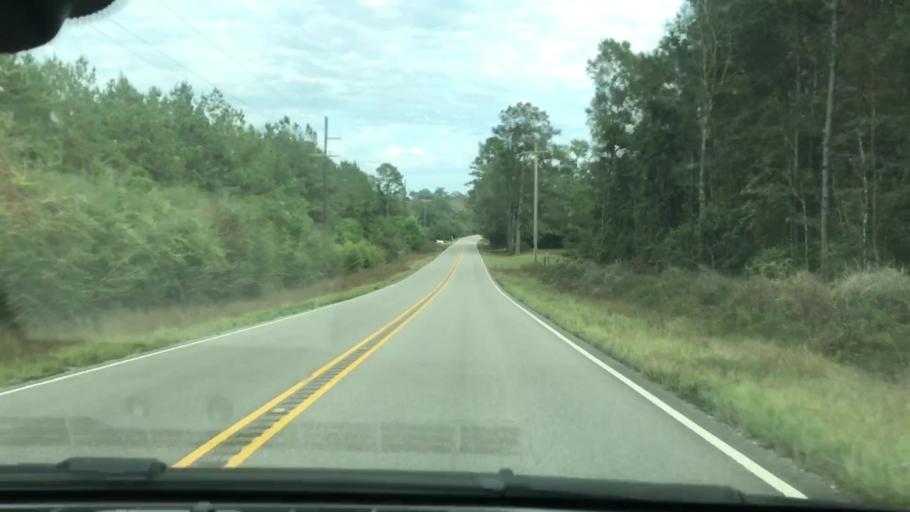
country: US
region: Louisiana
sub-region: Saint Tammany Parish
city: Abita Springs
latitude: 30.5340
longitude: -89.9032
